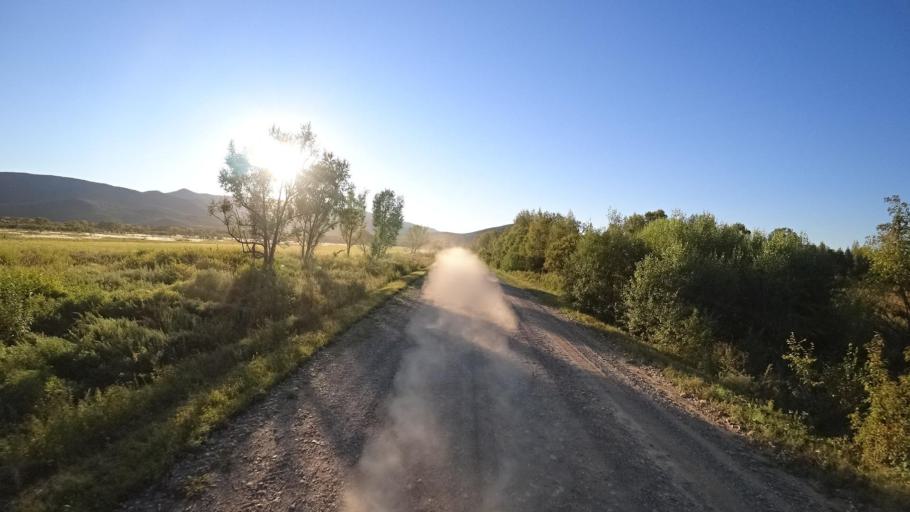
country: RU
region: Primorskiy
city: Kirovskiy
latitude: 44.8262
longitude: 133.5952
